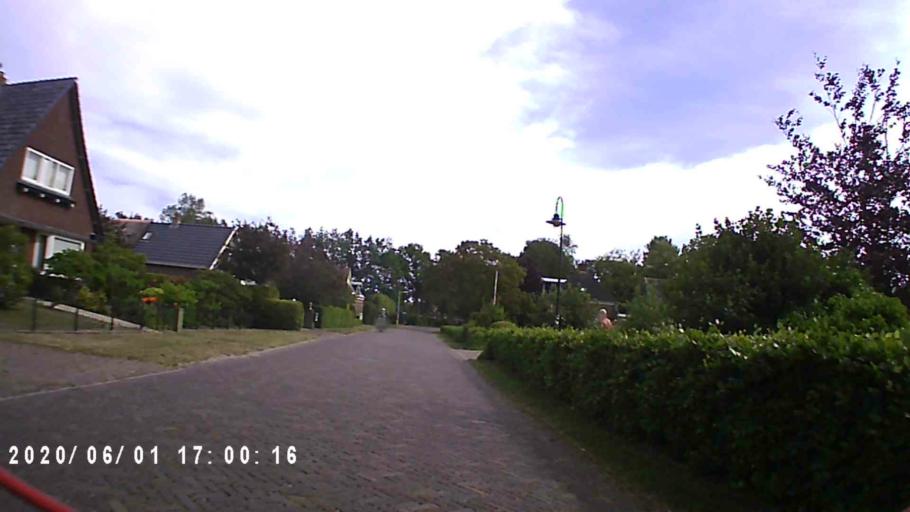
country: NL
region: Friesland
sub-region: Gemeente Tytsjerksteradiel
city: Hurdegaryp
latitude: 53.1835
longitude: 5.9293
